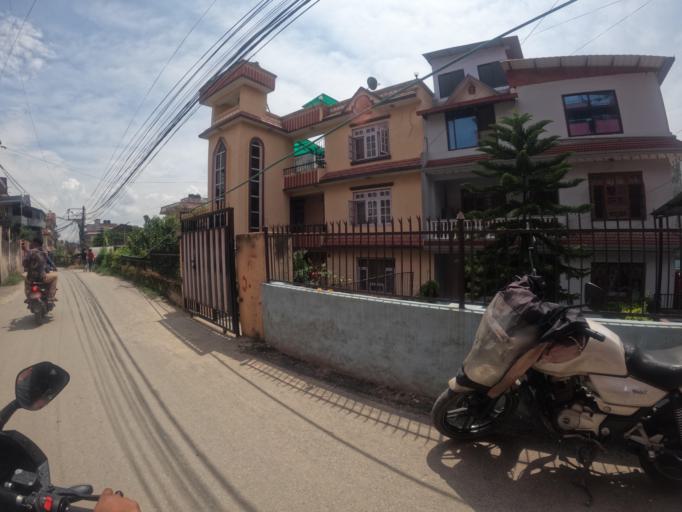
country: NP
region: Central Region
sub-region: Bagmati Zone
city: Kathmandu
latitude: 27.6807
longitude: 85.3673
